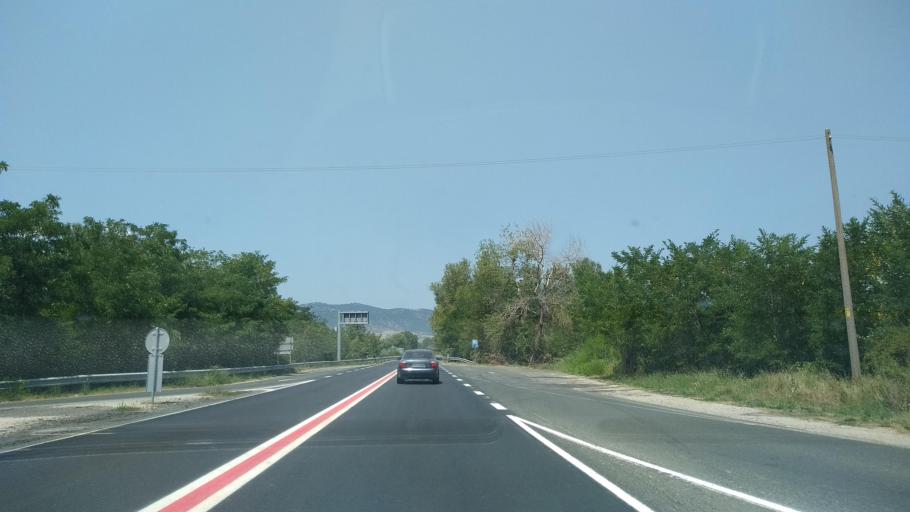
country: BG
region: Blagoevgrad
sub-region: Obshtina Simitli
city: Simitli
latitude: 41.8536
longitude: 23.1366
